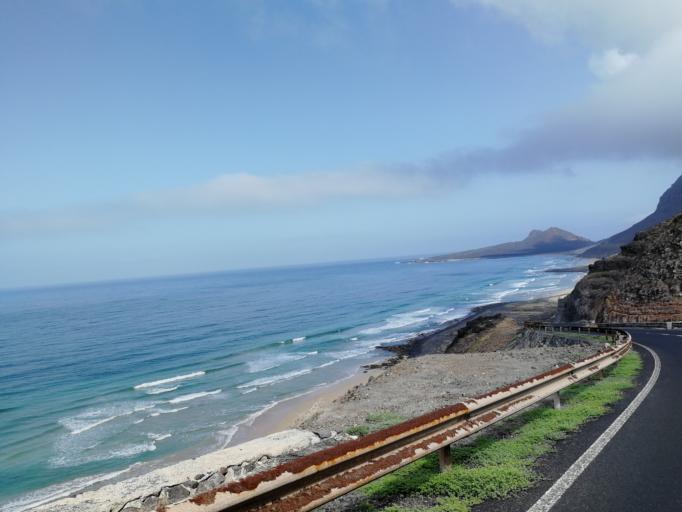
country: CV
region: Sao Vicente
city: Mindelo
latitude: 16.8663
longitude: -24.8973
